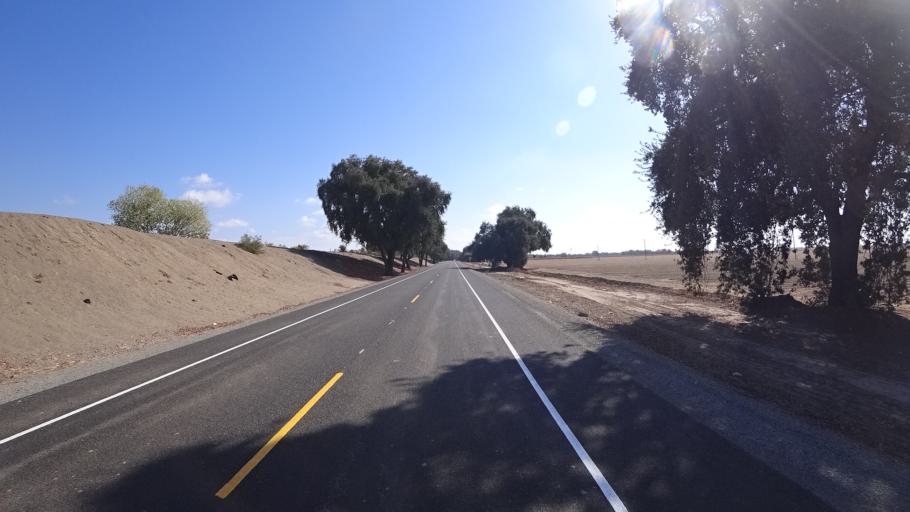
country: US
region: California
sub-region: Yolo County
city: West Sacramento
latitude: 38.6696
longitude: -121.6238
